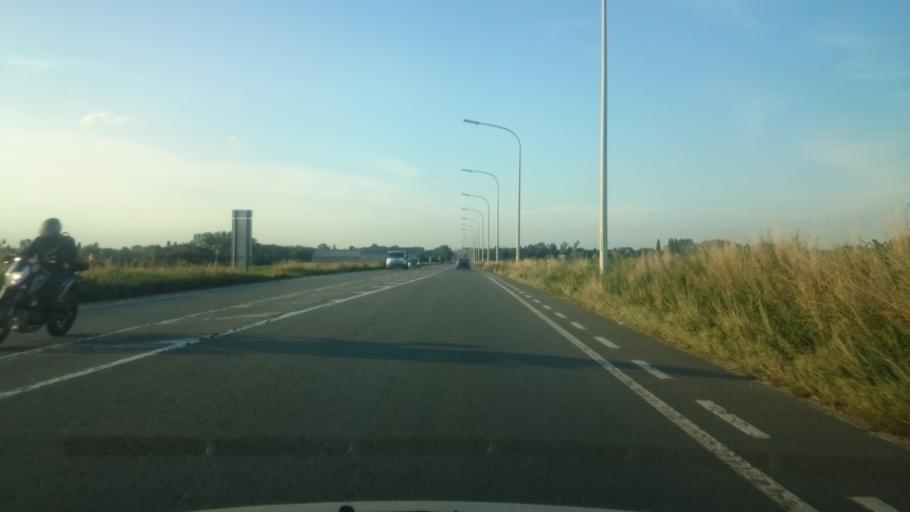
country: BE
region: Wallonia
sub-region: Province de Namur
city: Gembloux
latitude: 50.5848
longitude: 4.6836
